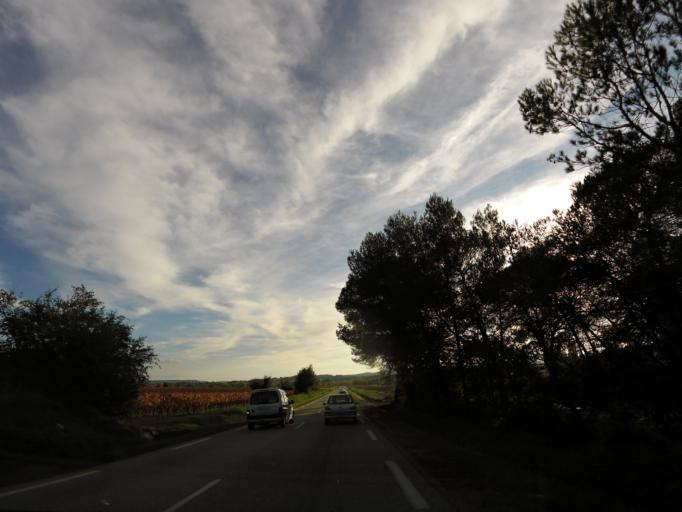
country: FR
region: Languedoc-Roussillon
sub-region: Departement du Gard
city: Ledignan
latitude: 43.9807
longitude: 4.1039
